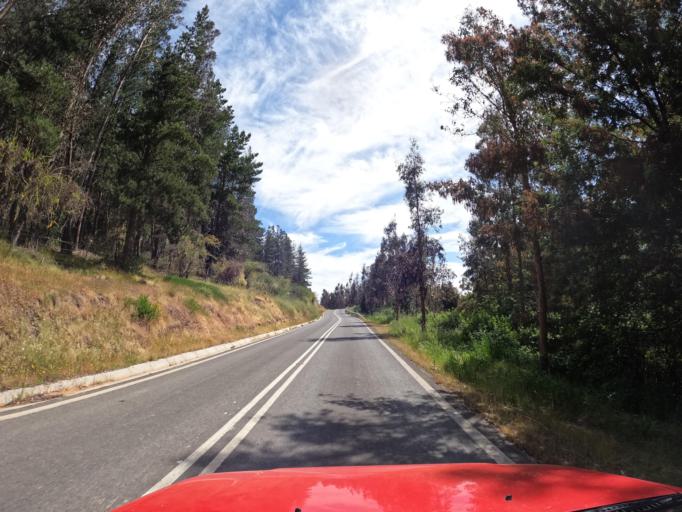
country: CL
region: Maule
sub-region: Provincia de Talca
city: Talca
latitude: -34.9932
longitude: -71.8731
